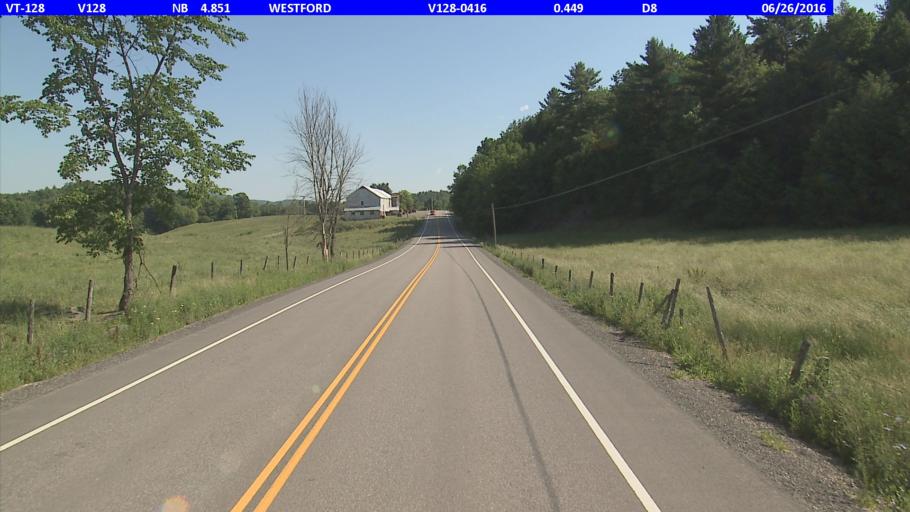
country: US
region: Vermont
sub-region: Chittenden County
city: Jericho
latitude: 44.5648
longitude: -73.0239
